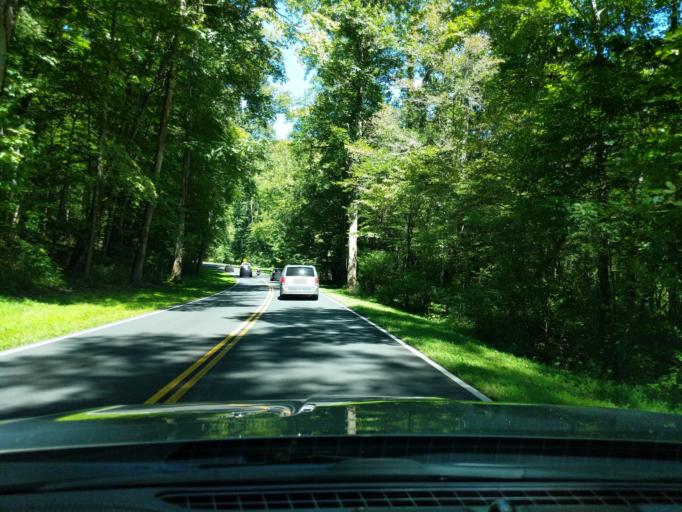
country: US
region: North Carolina
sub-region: Swain County
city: Cherokee
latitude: 35.5382
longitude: -83.3005
